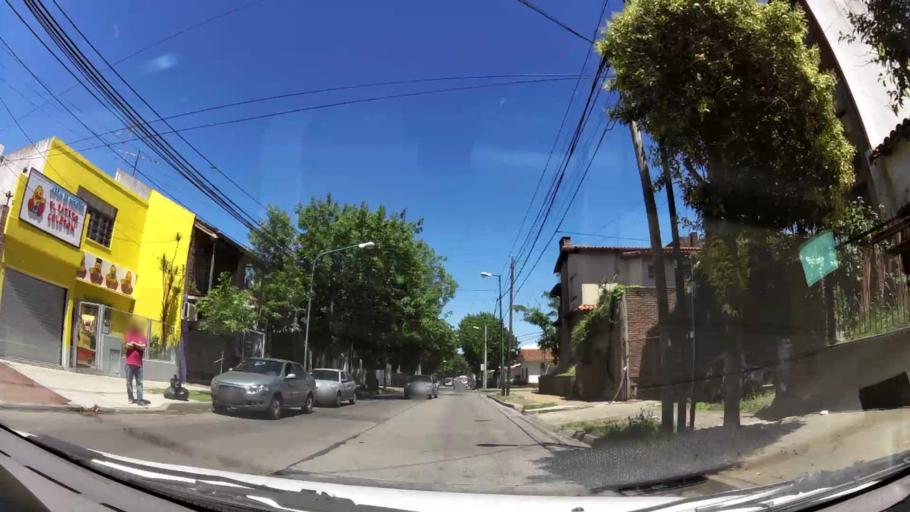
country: AR
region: Buenos Aires
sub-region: Partido de Vicente Lopez
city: Olivos
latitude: -34.4984
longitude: -58.4991
